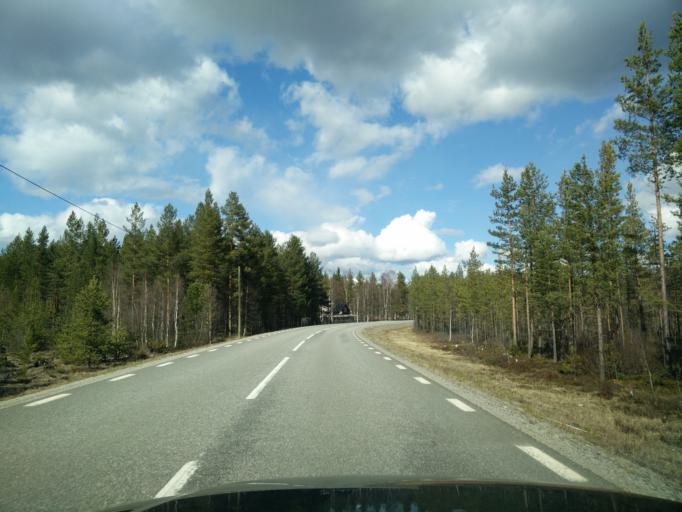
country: SE
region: Jaemtland
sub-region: Braecke Kommun
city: Braecke
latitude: 62.4565
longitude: 14.9572
